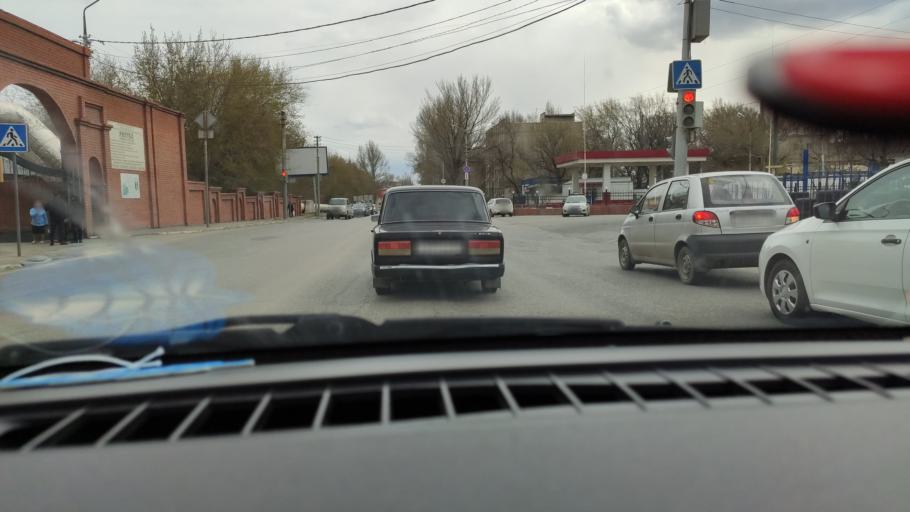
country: RU
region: Saratov
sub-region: Saratovskiy Rayon
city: Saratov
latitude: 51.5545
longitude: 46.0080
